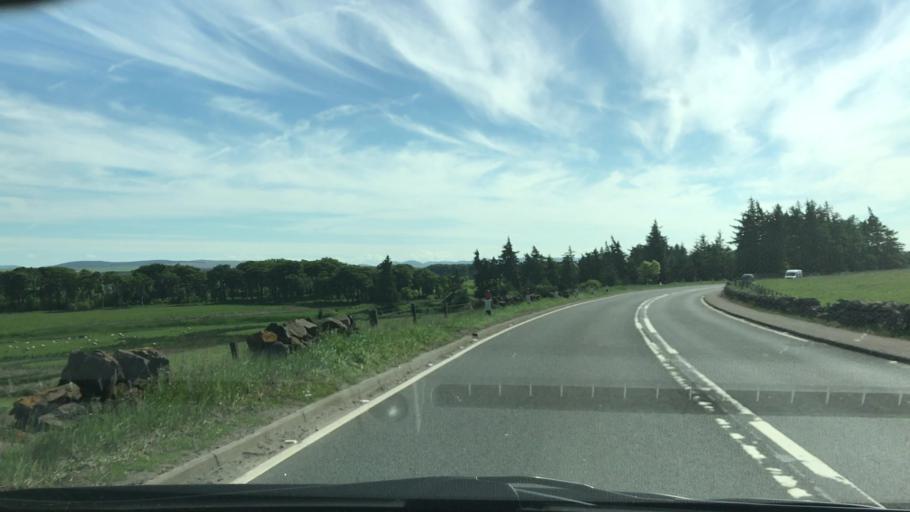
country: GB
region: Scotland
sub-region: Midlothian
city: Penicuik
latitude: 55.8223
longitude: -3.2832
